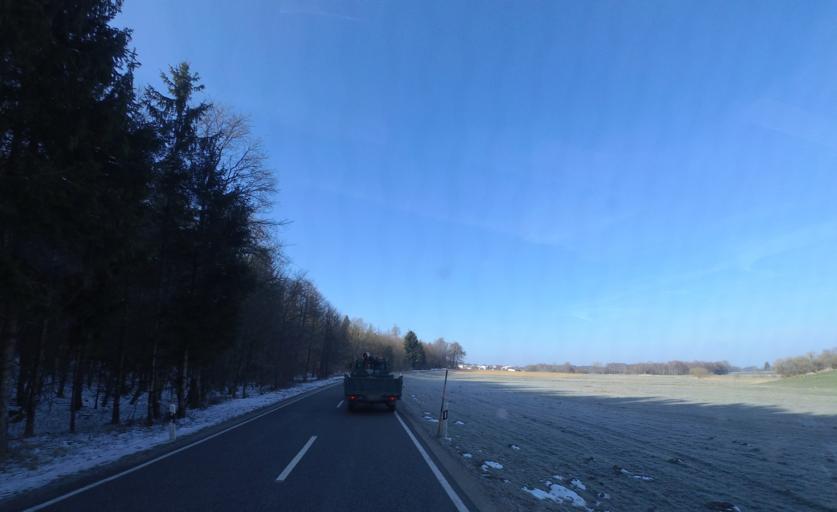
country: DE
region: Bavaria
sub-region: Upper Bavaria
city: Chieming
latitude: 47.9381
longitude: 12.5374
